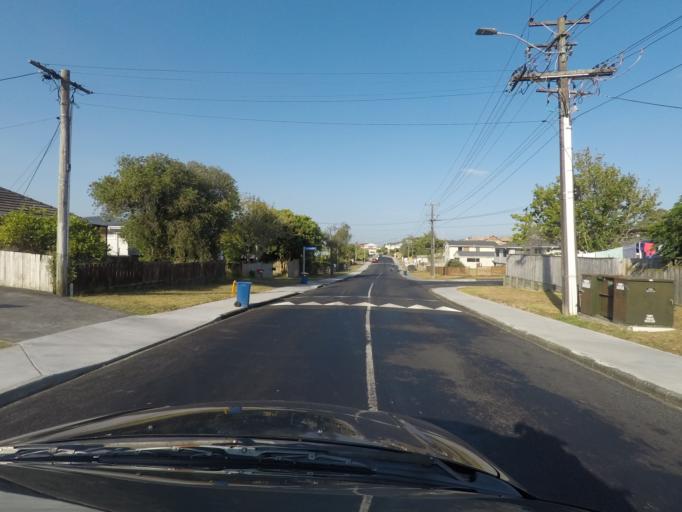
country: NZ
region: Auckland
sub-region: Auckland
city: Rosebank
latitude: -36.8592
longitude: 174.6480
